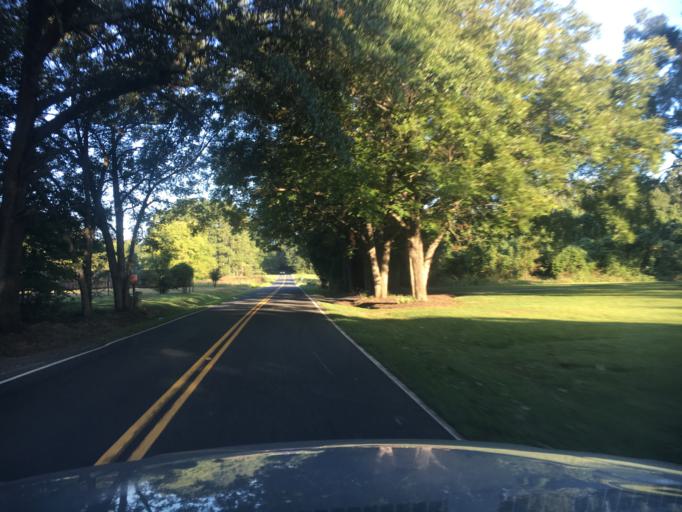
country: US
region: South Carolina
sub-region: Spartanburg County
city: Woodruff
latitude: 34.6345
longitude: -81.9876
